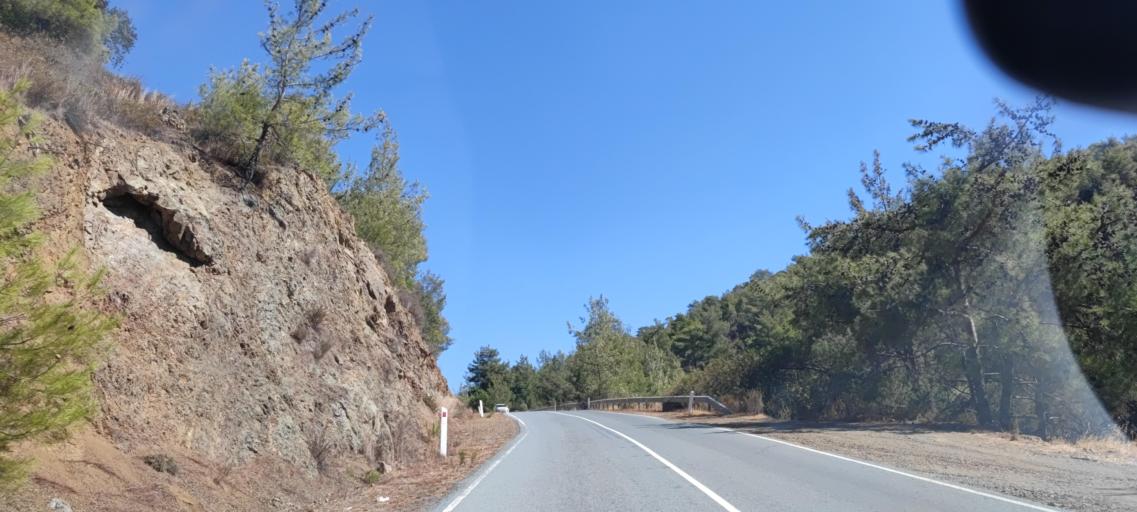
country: CY
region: Limassol
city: Pelendri
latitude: 34.8260
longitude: 33.0187
